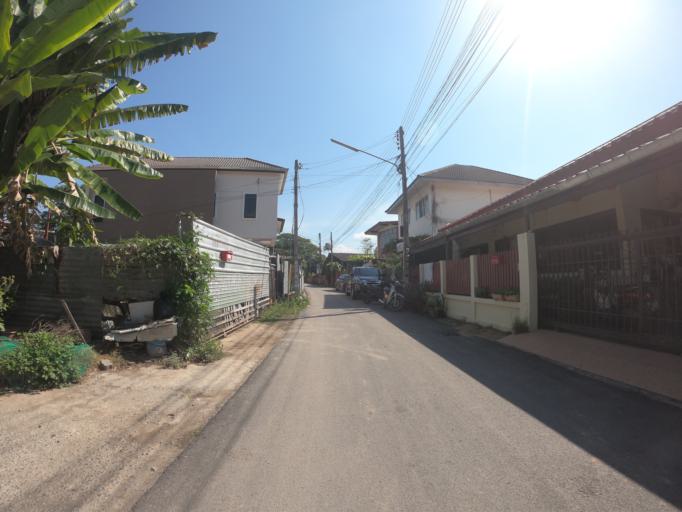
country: TH
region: Chiang Mai
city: Chiang Mai
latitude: 18.7776
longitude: 98.9820
